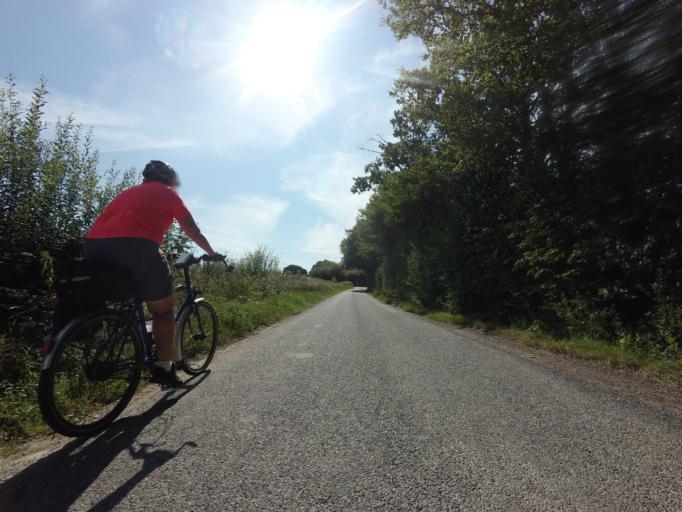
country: GB
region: England
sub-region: East Sussex
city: Rye
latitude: 50.9805
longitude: 0.7183
